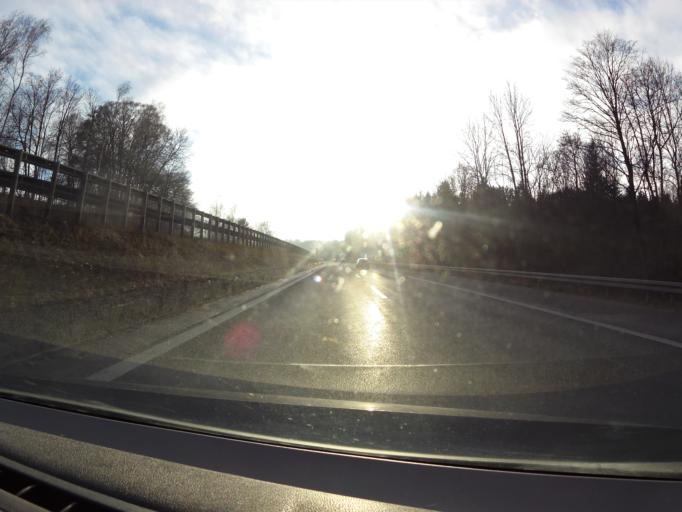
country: DE
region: Bavaria
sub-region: Upper Bavaria
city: Icking
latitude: 47.9430
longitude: 11.4068
